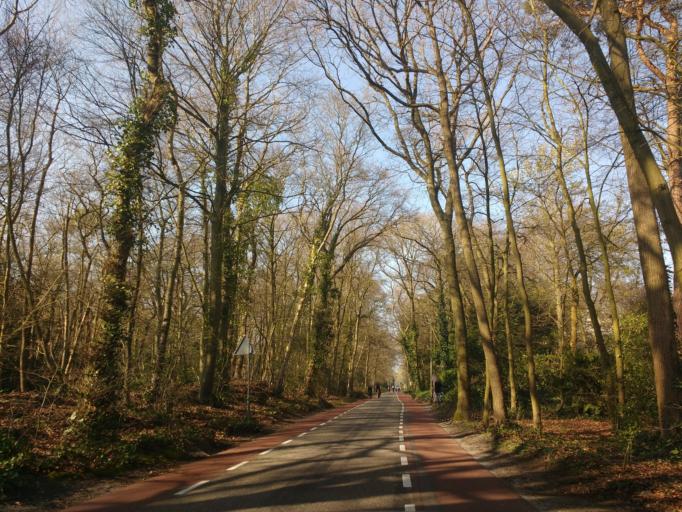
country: NL
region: North Holland
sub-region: Gemeente Heiloo
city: Heiloo
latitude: 52.6672
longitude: 4.6930
